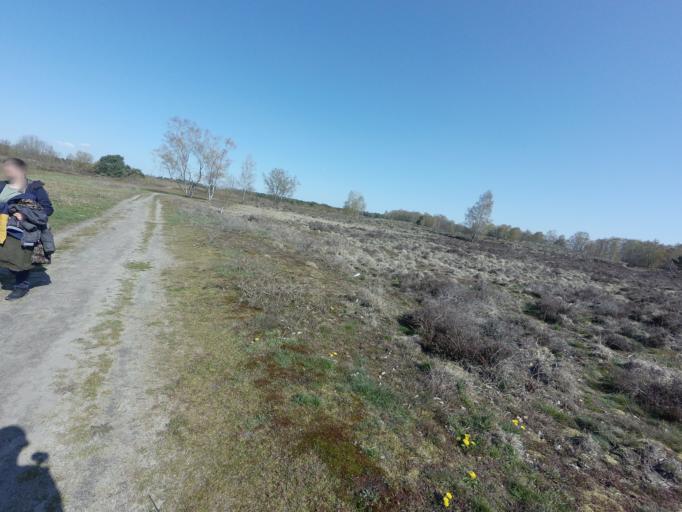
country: NL
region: Limburg
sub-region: Gemeente Bergen
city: Wellerlooi
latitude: 51.6050
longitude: 6.0703
